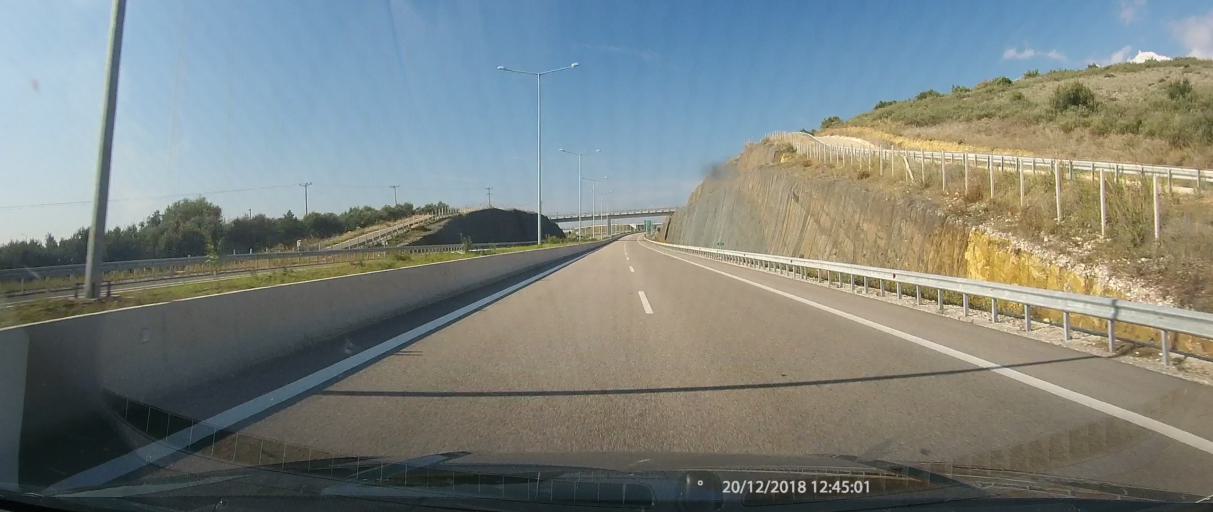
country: GR
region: West Greece
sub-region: Nomos Aitolias kai Akarnanias
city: Galatas
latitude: 38.3775
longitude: 21.5080
